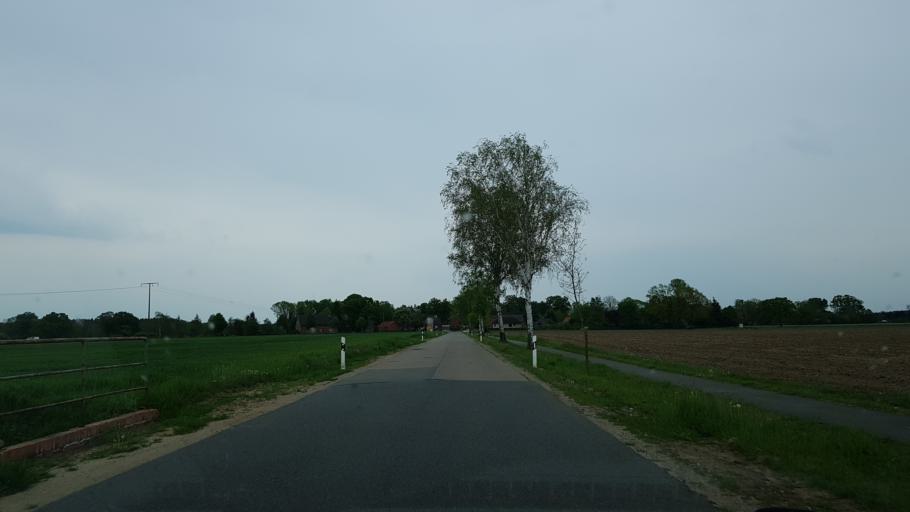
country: DE
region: Lower Saxony
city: Gartow
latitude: 53.0464
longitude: 11.4415
